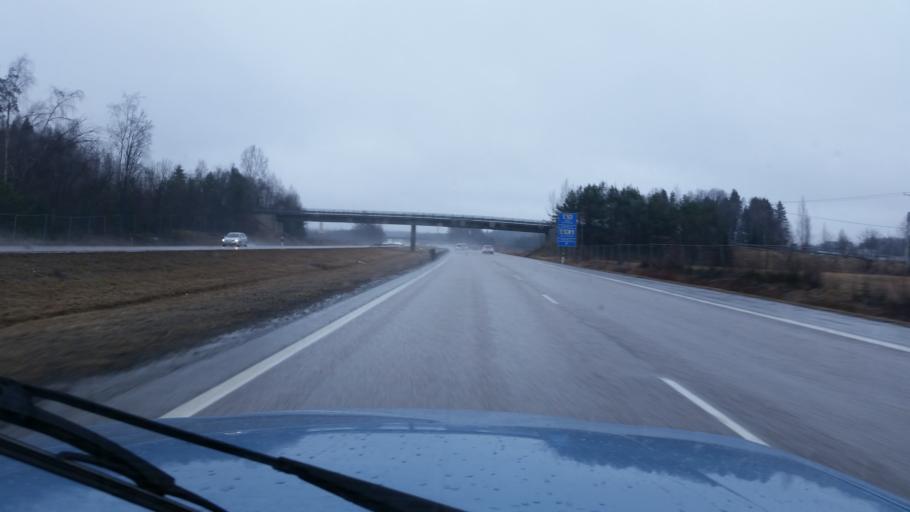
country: FI
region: Uusimaa
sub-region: Helsinki
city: Hyvinge
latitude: 60.6099
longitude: 24.8044
